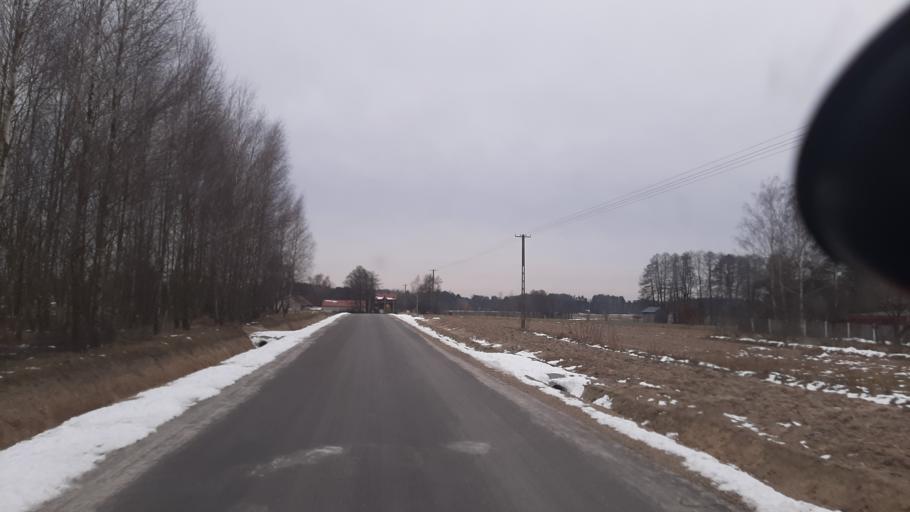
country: PL
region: Lublin Voivodeship
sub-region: Powiat lubartowski
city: Kamionka
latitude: 51.5120
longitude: 22.4593
